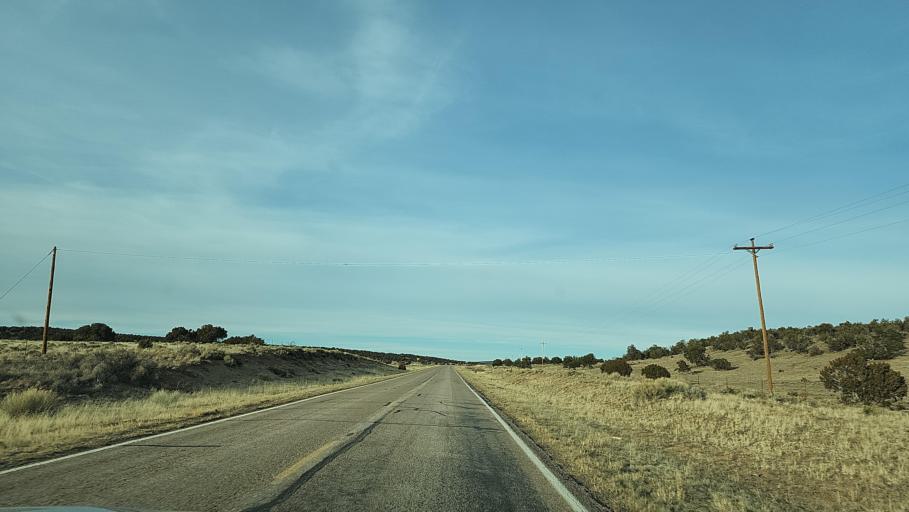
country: US
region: New Mexico
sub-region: Catron County
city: Reserve
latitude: 34.3943
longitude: -108.4461
